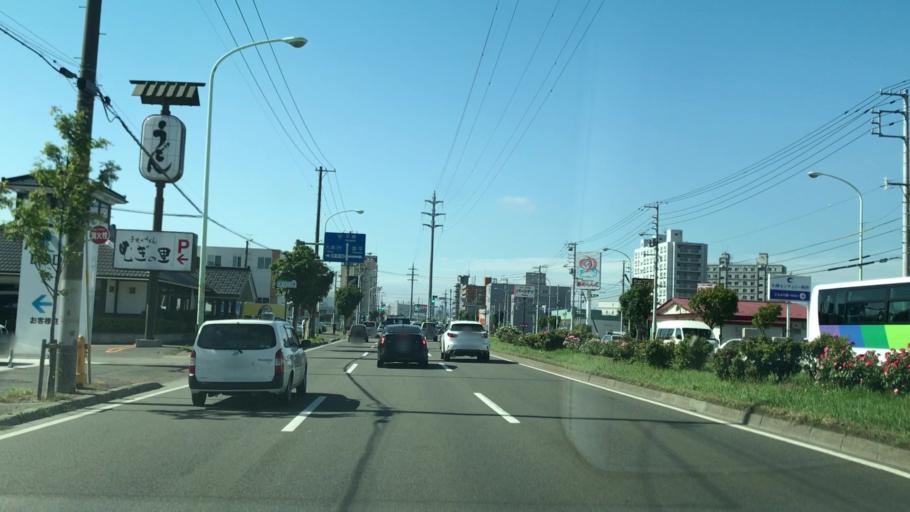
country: JP
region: Hokkaido
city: Sapporo
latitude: 43.0690
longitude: 141.4088
